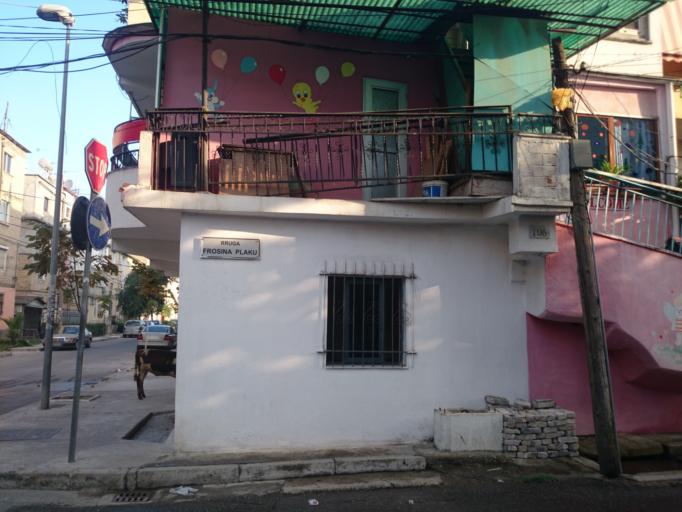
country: AL
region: Tirane
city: Tirana
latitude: 41.3261
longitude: 19.7941
